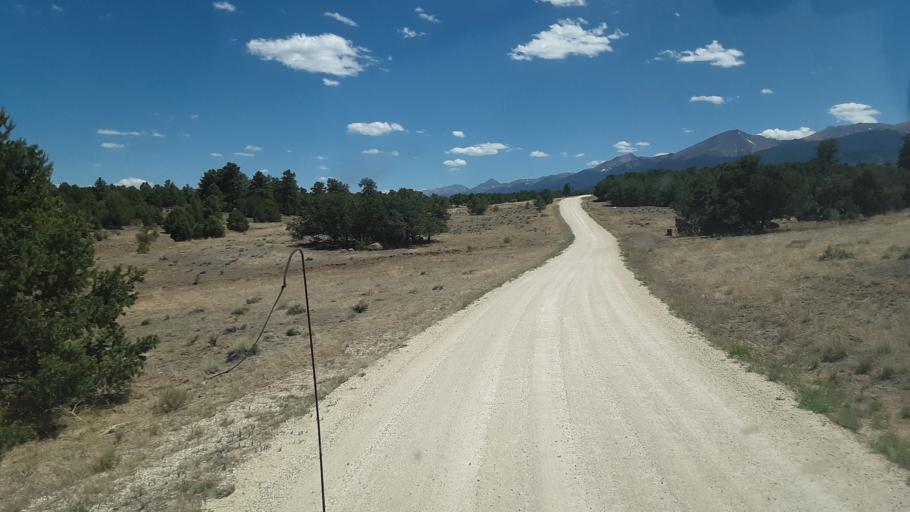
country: US
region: Colorado
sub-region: Custer County
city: Westcliffe
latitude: 38.3214
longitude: -105.6248
